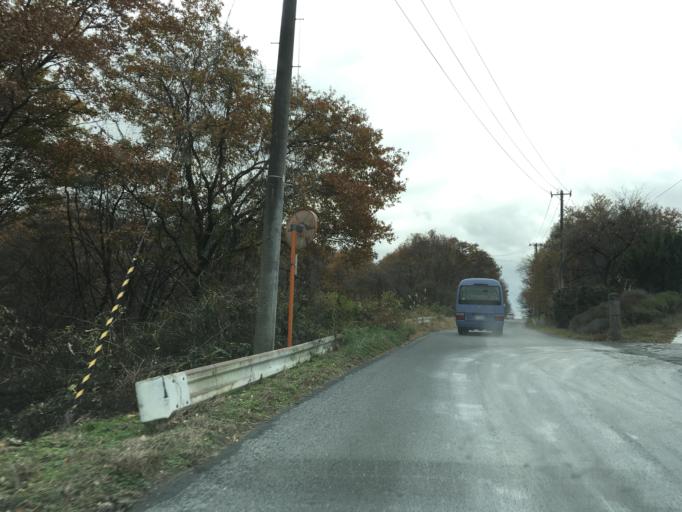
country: JP
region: Iwate
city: Ichinoseki
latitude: 38.8470
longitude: 141.0517
